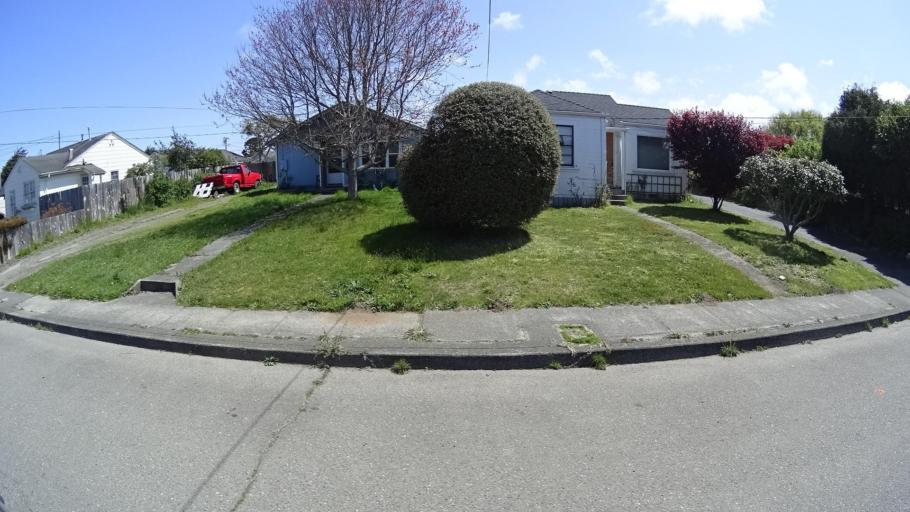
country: US
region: California
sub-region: Humboldt County
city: Bayview
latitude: 40.7785
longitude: -124.1748
